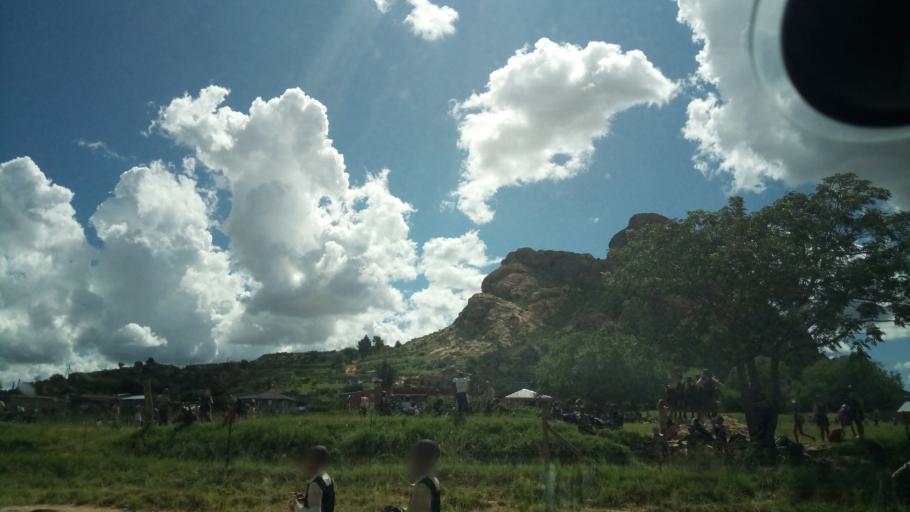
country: LS
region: Maseru
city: Maseru
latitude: -29.3548
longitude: 27.5351
